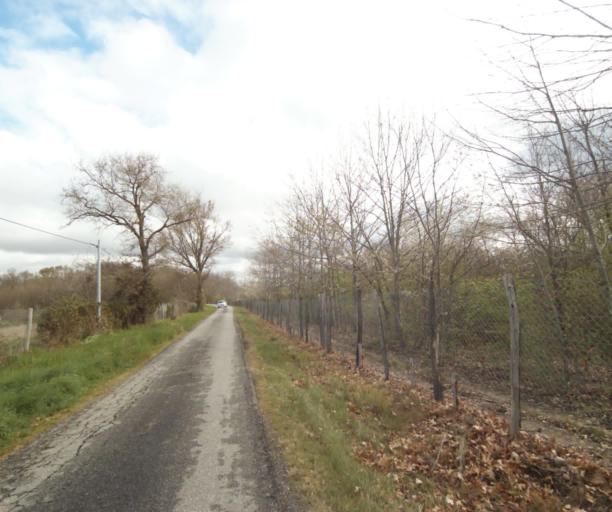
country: FR
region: Midi-Pyrenees
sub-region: Departement de l'Ariege
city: Saverdun
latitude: 43.2086
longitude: 1.5612
